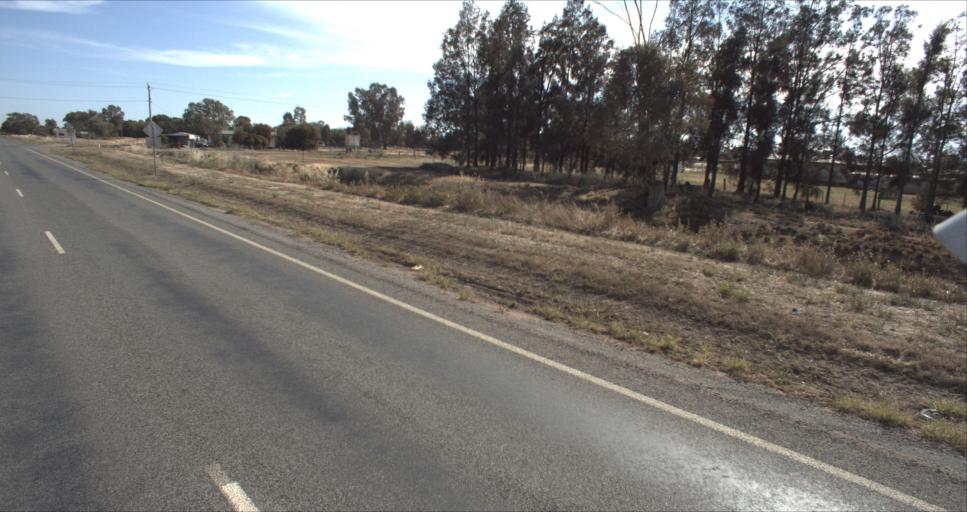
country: AU
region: New South Wales
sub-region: Leeton
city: Leeton
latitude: -34.5966
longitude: 146.4055
